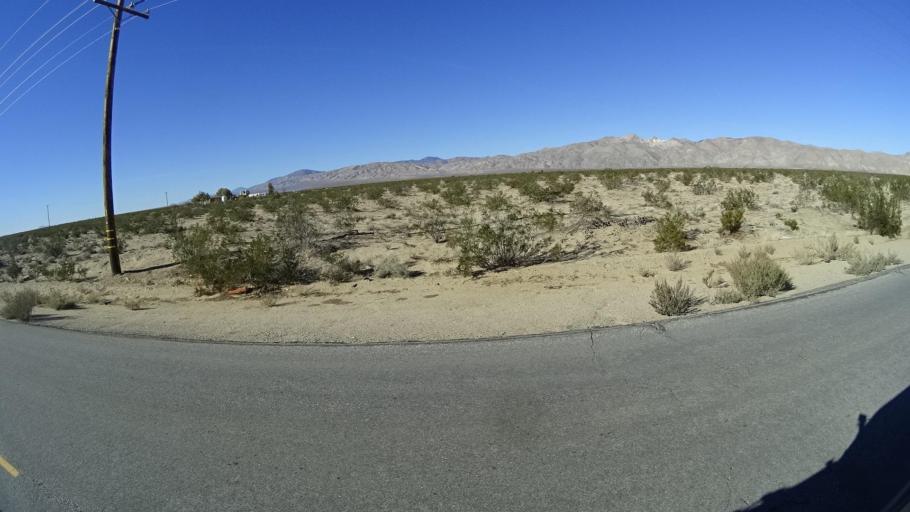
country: US
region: California
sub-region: Kern County
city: California City
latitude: 35.2347
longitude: -117.9859
